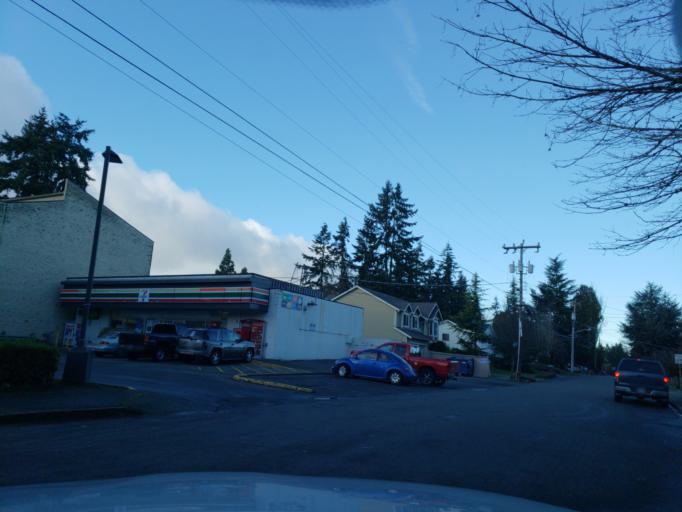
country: US
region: Washington
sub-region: King County
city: Shoreline
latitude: 47.7634
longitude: -122.3422
